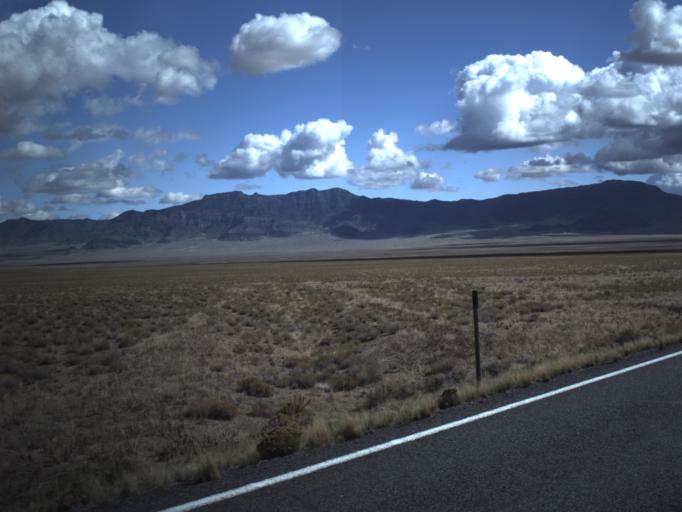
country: US
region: Utah
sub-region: Beaver County
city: Milford
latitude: 38.5615
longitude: -113.7609
